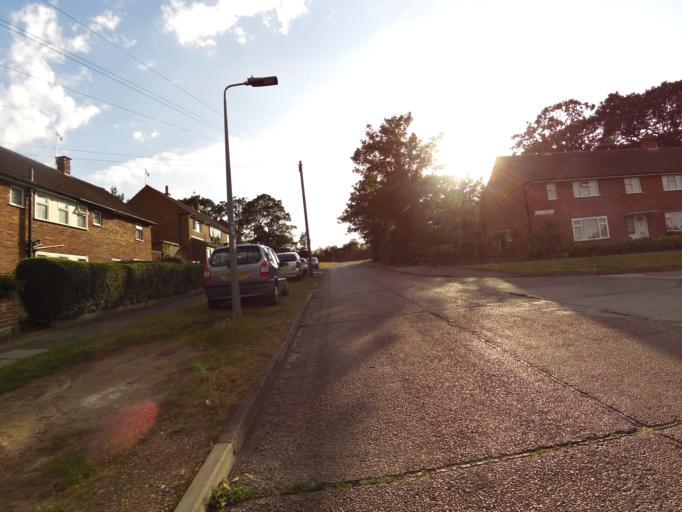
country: GB
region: England
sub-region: Suffolk
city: Ipswich
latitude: 52.0499
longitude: 1.1249
